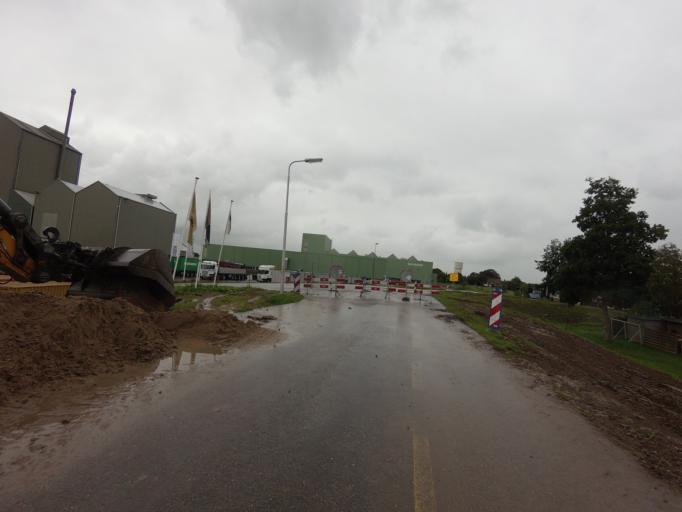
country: NL
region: South Holland
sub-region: Molenwaard
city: Nieuw-Lekkerland
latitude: 51.8917
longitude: 4.6887
